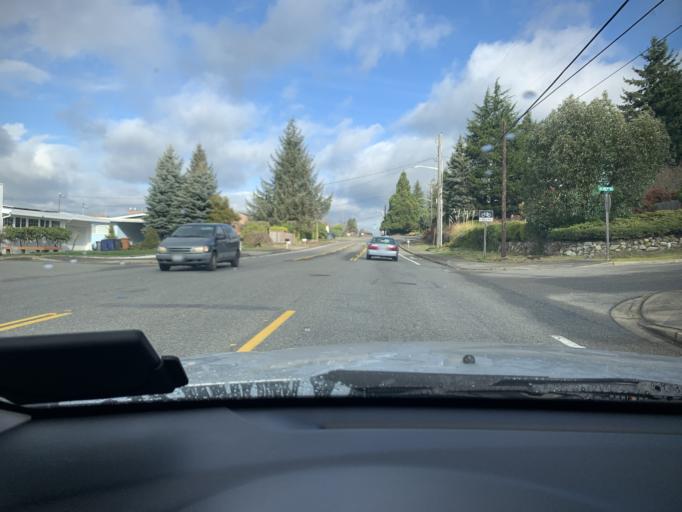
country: US
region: Washington
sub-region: Pierce County
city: University Place
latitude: 47.2634
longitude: -122.5371
